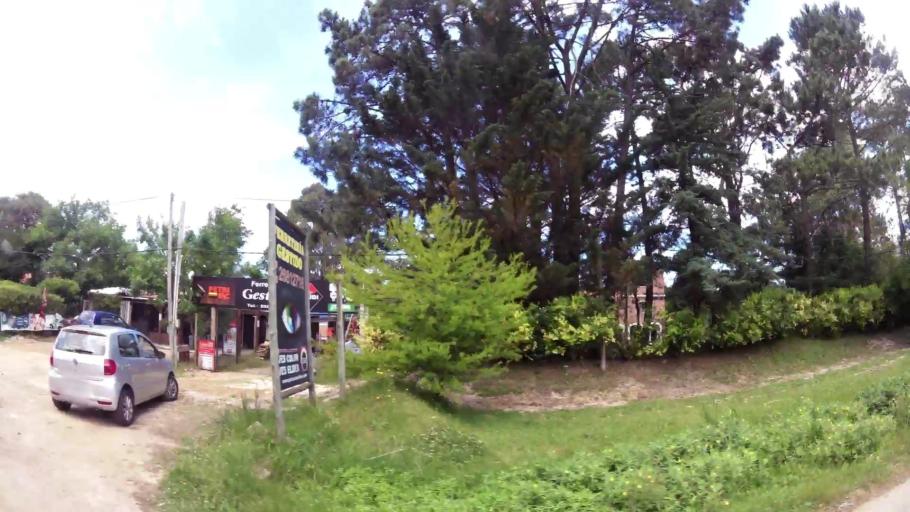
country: UY
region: Canelones
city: Empalme Olmos
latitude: -34.7955
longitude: -55.8853
